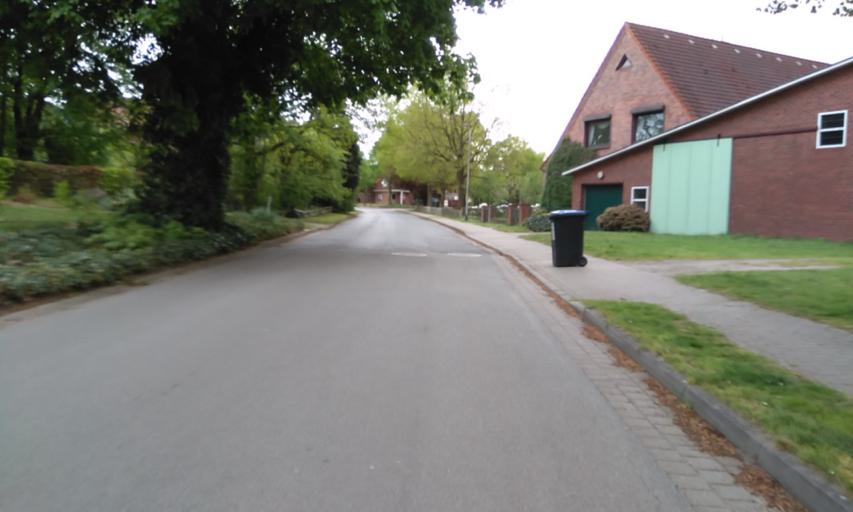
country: DE
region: Lower Saxony
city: Nottensdorf
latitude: 53.4864
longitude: 9.6046
